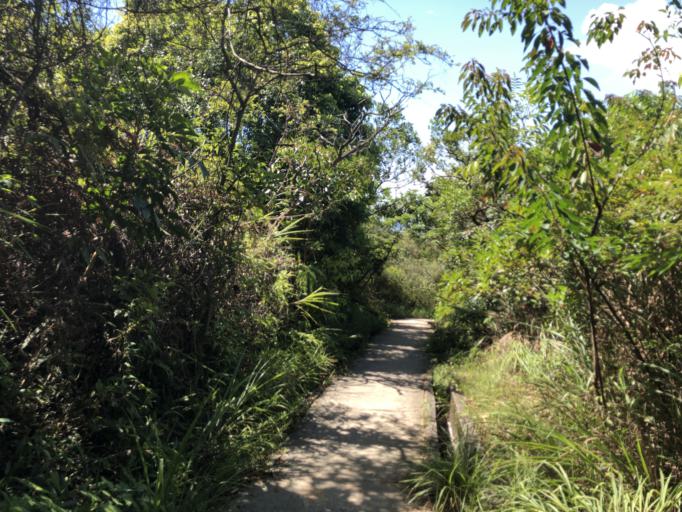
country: HK
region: Tuen Mun
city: Tuen Mun
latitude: 22.2883
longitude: 113.9809
